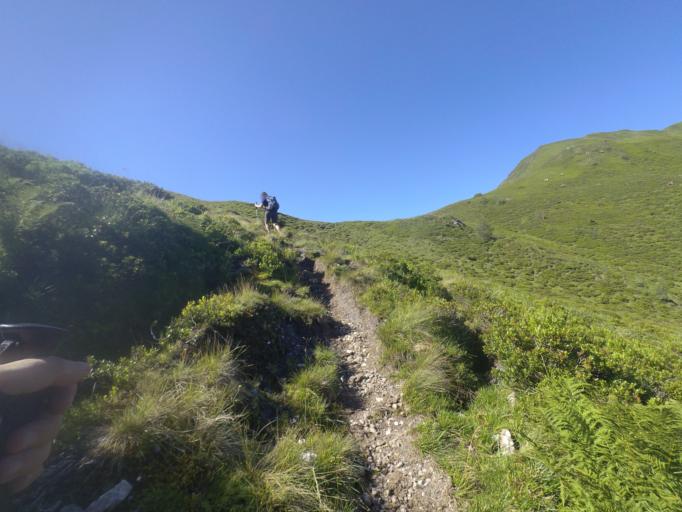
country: AT
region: Salzburg
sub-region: Politischer Bezirk Sankt Johann im Pongau
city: Dorfgastein
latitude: 47.2356
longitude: 13.0618
